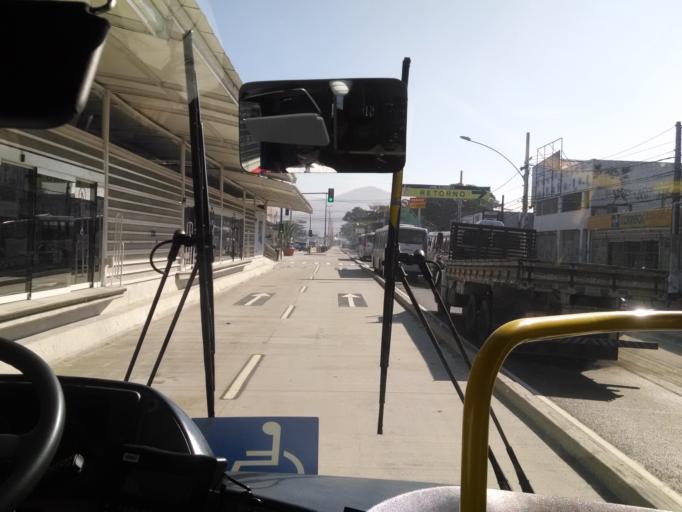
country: BR
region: Rio de Janeiro
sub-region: Sao Joao De Meriti
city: Sao Joao de Meriti
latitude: -22.9297
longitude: -43.3734
